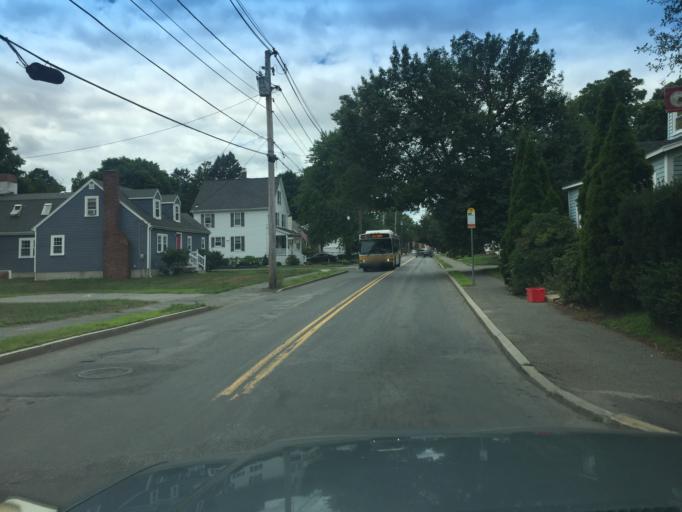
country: US
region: Massachusetts
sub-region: Middlesex County
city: Reading
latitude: 42.5210
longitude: -71.0999
